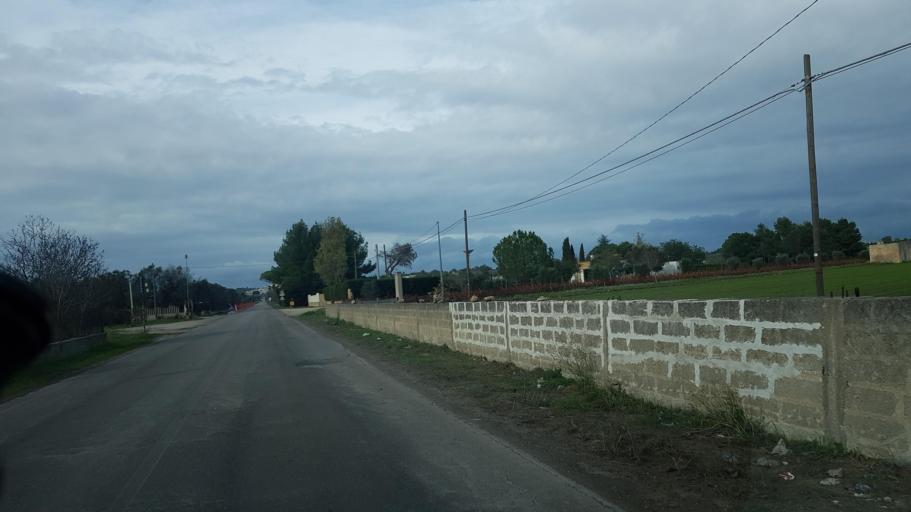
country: IT
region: Apulia
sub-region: Provincia di Brindisi
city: Oria
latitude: 40.4867
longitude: 17.6714
